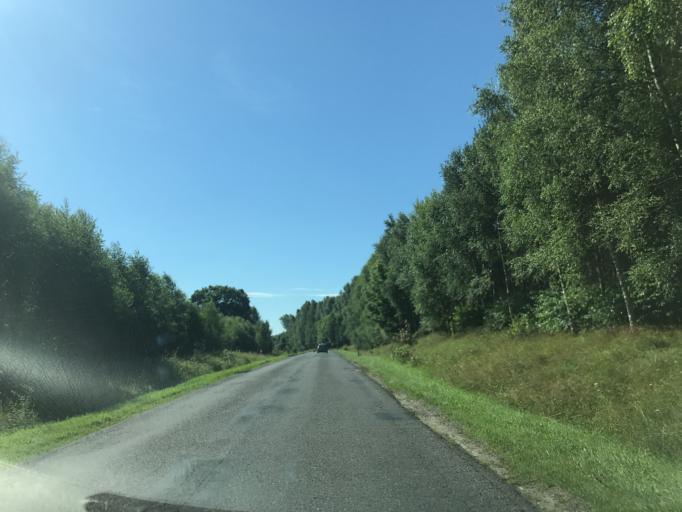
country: PL
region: Pomeranian Voivodeship
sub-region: Powiat bytowski
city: Czarna Dabrowka
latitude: 54.3721
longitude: 17.5010
